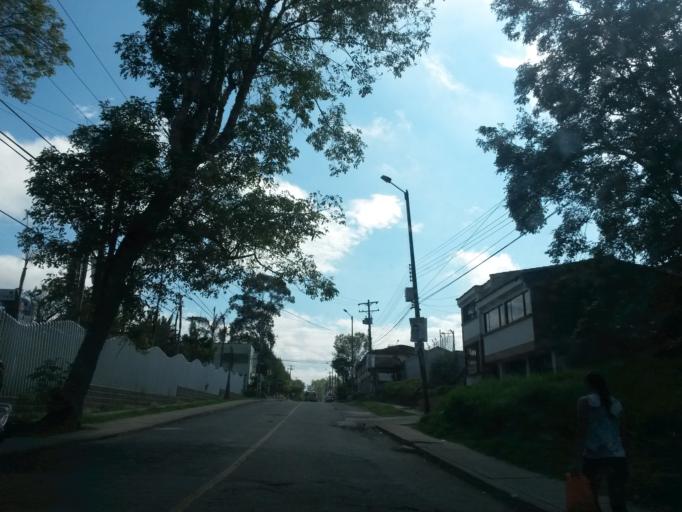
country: CO
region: Cauca
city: Popayan
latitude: 2.4588
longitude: -76.6031
